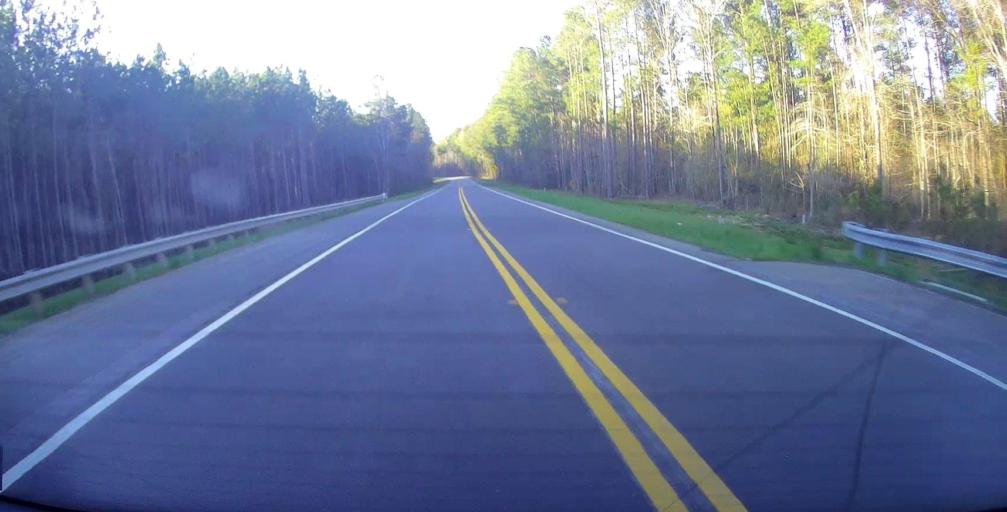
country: US
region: Georgia
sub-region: Wilcox County
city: Abbeville
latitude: 32.0853
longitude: -83.2918
